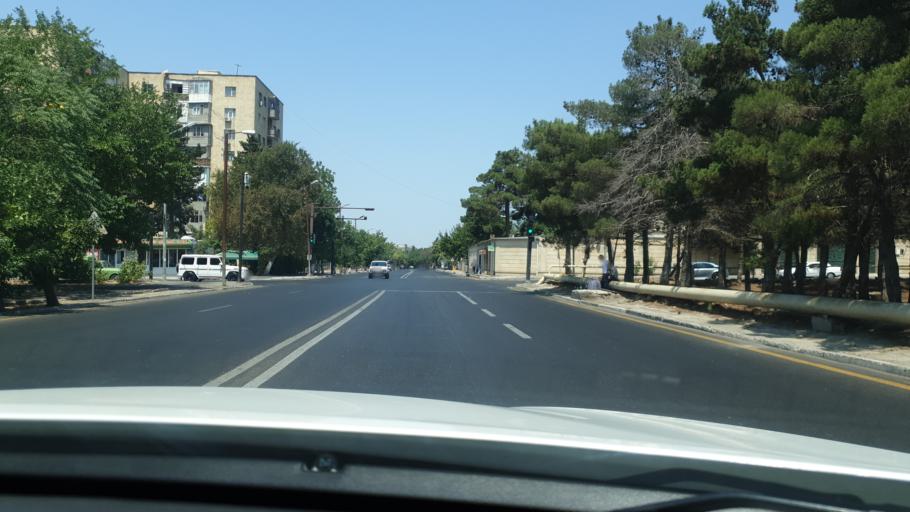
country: AZ
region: Baki
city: Bakixanov
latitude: 40.4161
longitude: 49.9473
